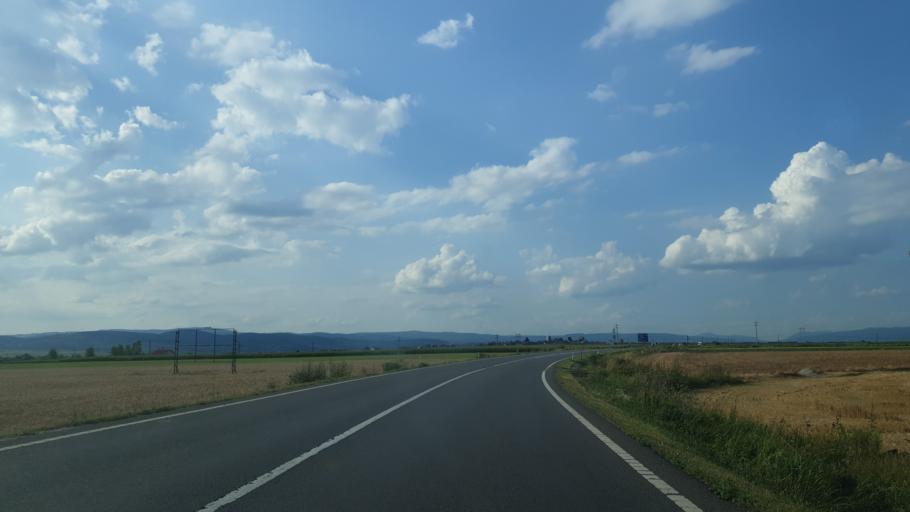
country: RO
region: Covasna
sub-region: Comuna Chichis
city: Chichis
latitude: 45.7944
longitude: 25.8046
